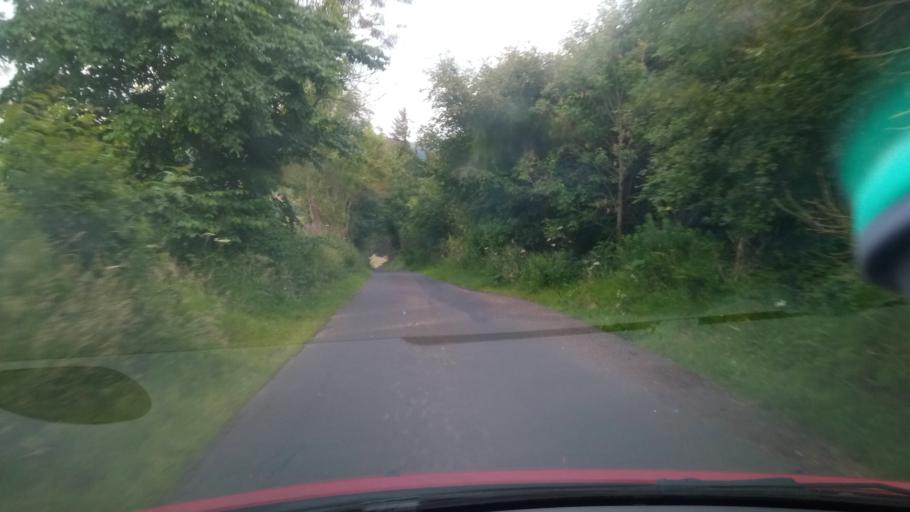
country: GB
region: Scotland
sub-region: The Scottish Borders
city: Saint Boswells
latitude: 55.5019
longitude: -2.6233
